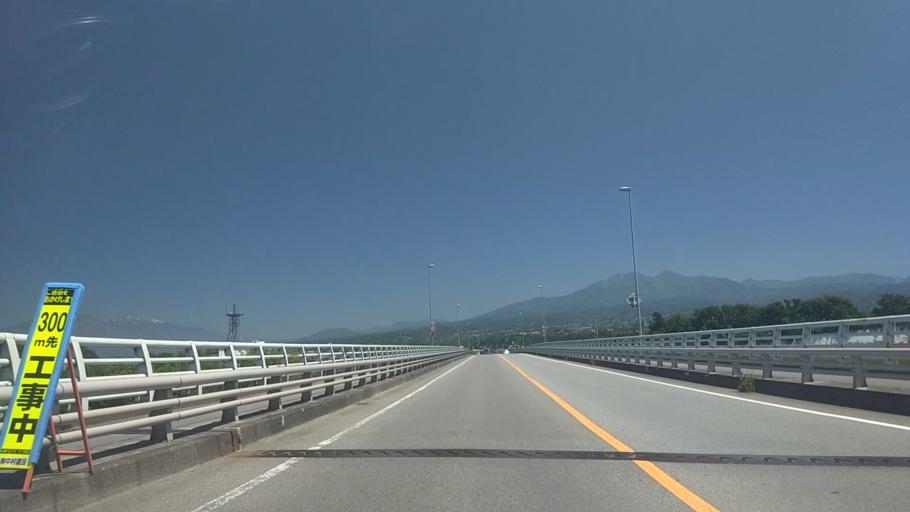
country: JP
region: Yamanashi
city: Nirasaki
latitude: 35.6994
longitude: 138.4534
